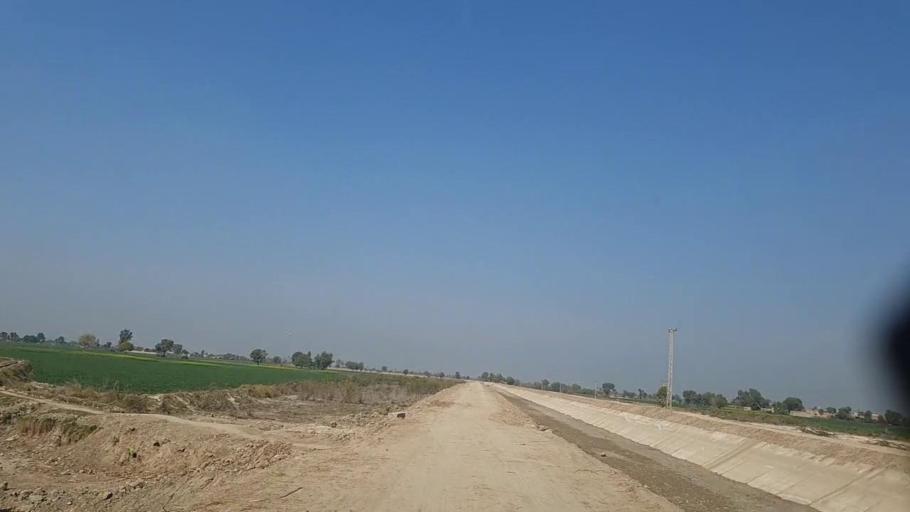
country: PK
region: Sindh
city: Sakrand
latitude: 26.1576
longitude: 68.3279
